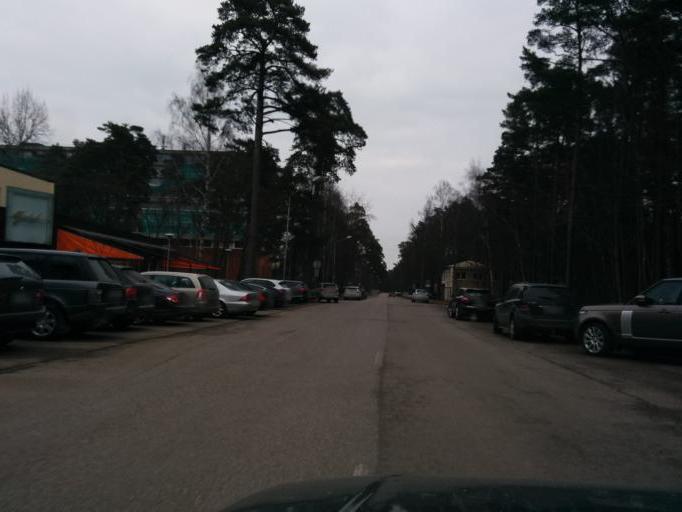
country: LV
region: Babite
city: Pinki
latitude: 56.9839
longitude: 23.8586
